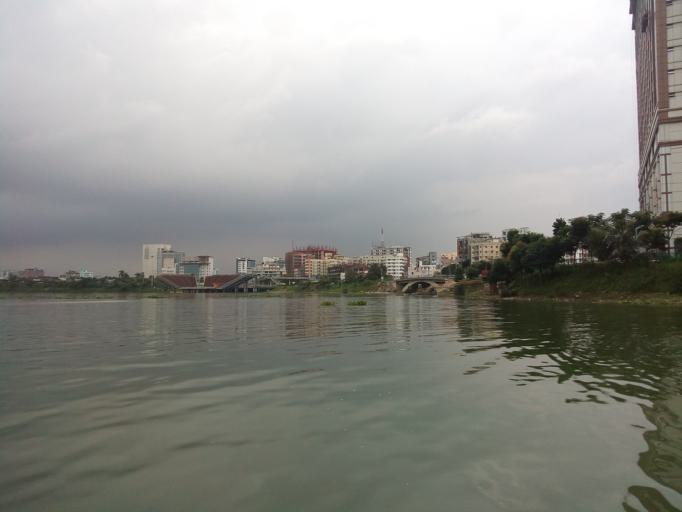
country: BD
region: Dhaka
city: Paltan
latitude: 23.7724
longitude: 90.4172
